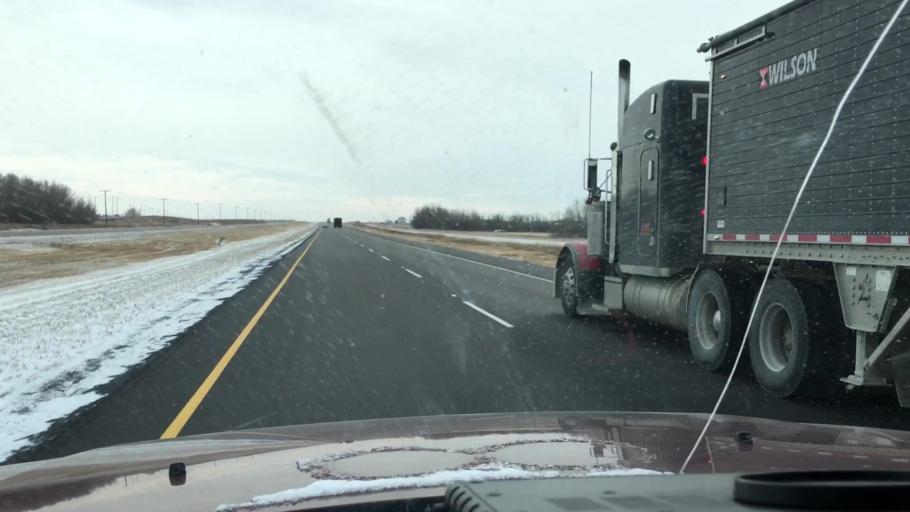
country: CA
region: Saskatchewan
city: Saskatoon
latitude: 51.9387
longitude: -106.5394
